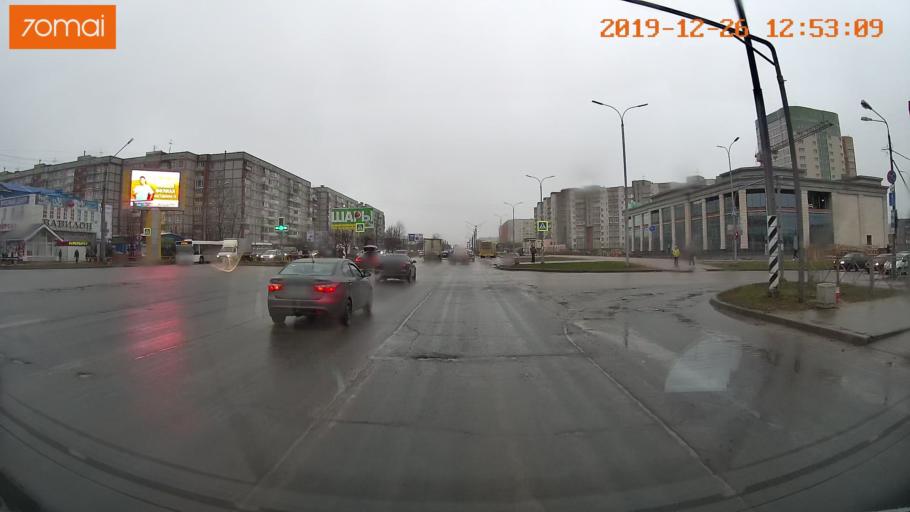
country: RU
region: Vologda
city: Cherepovets
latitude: 59.0985
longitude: 37.9105
